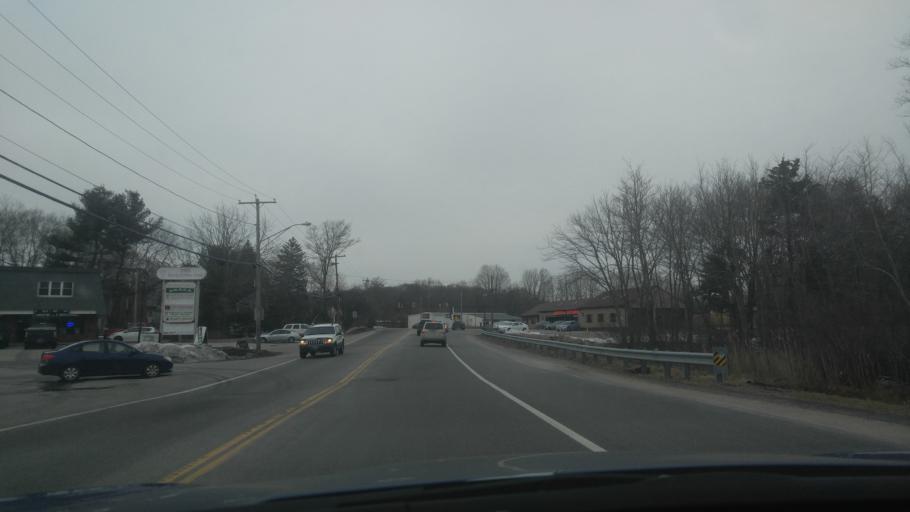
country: US
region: Rhode Island
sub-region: Kent County
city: West Warwick
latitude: 41.6890
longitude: -71.5606
